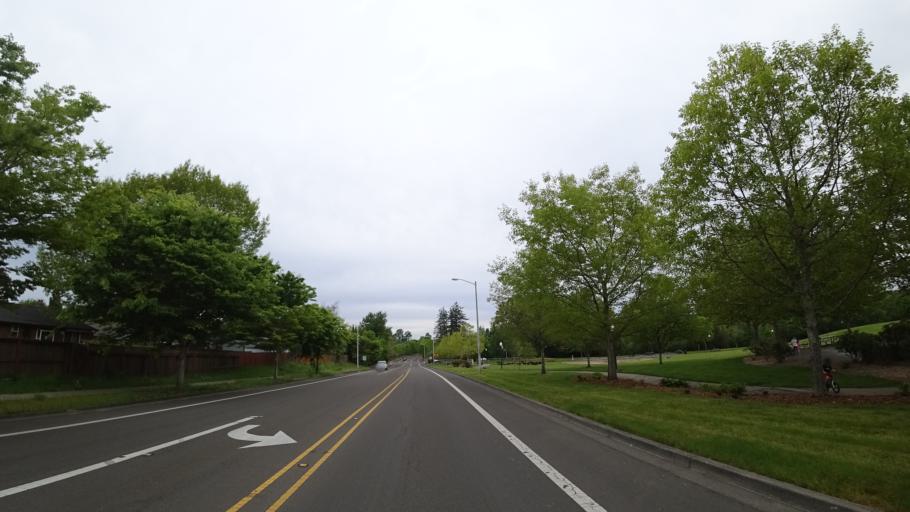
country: US
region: Oregon
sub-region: Washington County
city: Aloha
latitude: 45.5103
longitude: -122.9162
